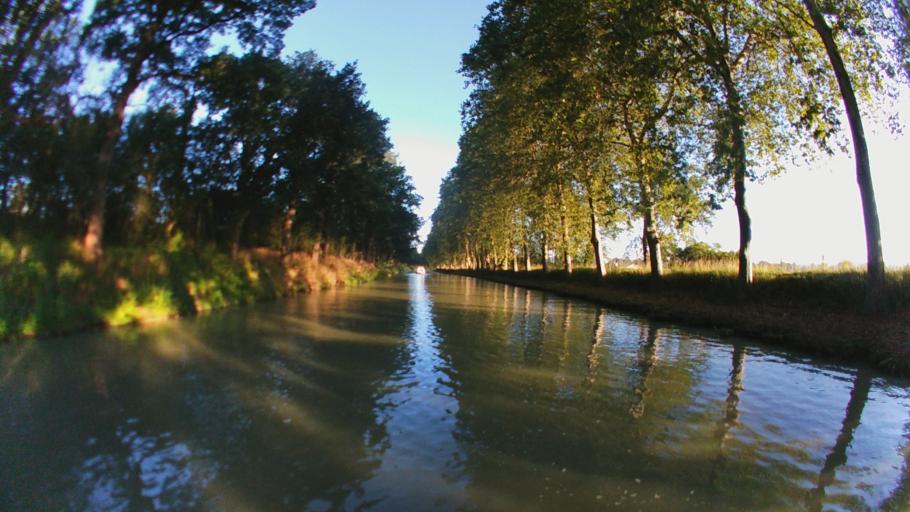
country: FR
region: Midi-Pyrenees
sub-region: Departement de la Haute-Garonne
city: Villenouvelle
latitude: 43.4143
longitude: 1.6460
